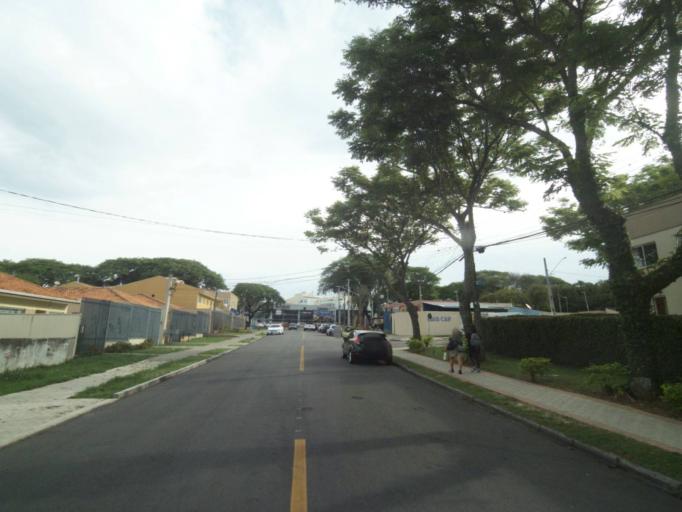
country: BR
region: Parana
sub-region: Curitiba
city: Curitiba
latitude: -25.4270
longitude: -49.2328
